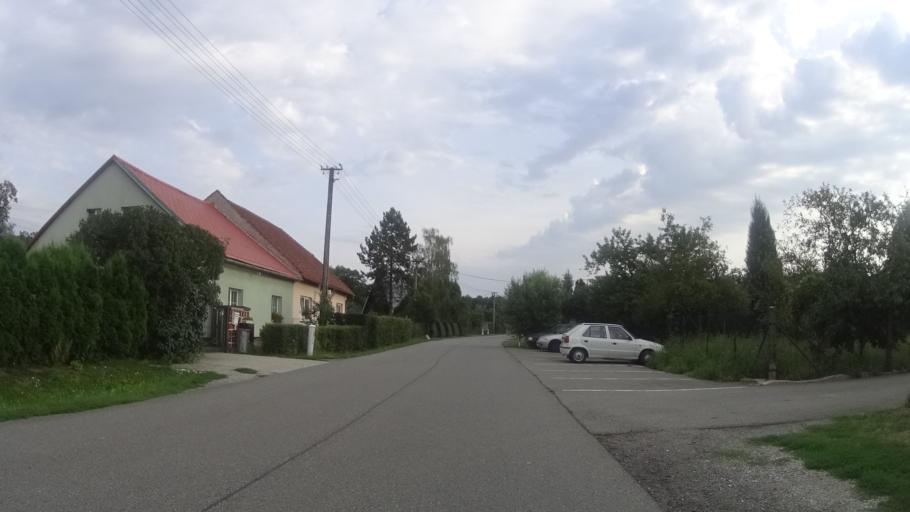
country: CZ
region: Zlin
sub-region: Okres Kromeriz
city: Kromeriz
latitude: 49.3174
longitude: 17.3877
